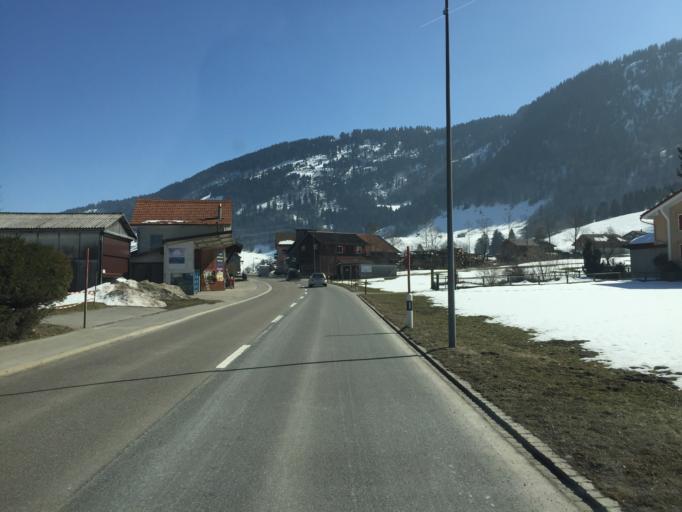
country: CH
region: Saint Gallen
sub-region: Wahlkreis Sarganserland
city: Quarten
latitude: 47.1861
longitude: 9.2482
